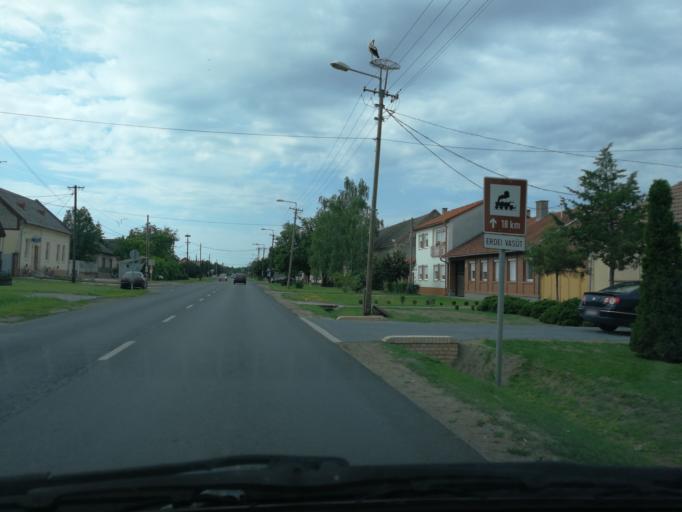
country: HU
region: Bacs-Kiskun
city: Ersekcsanad
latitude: 46.2518
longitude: 18.9787
